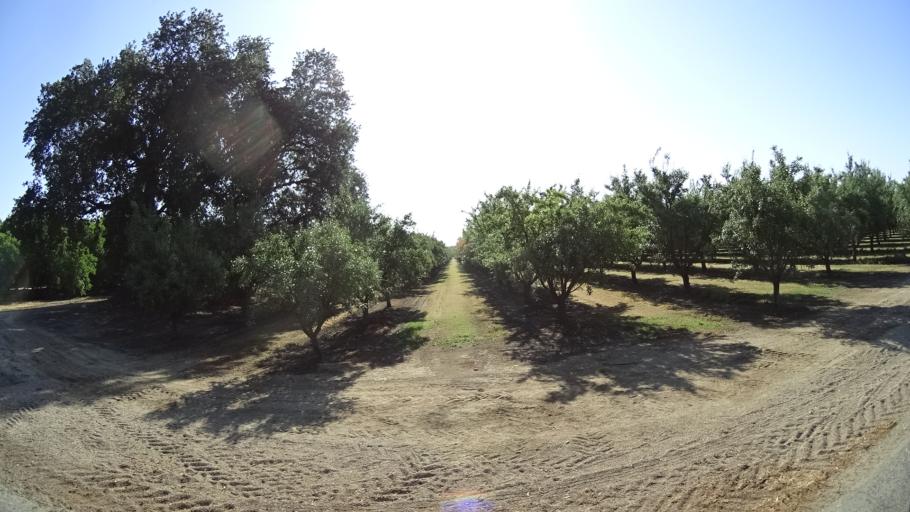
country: US
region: California
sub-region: Fresno County
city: Laton
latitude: 36.3981
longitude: -119.7181
